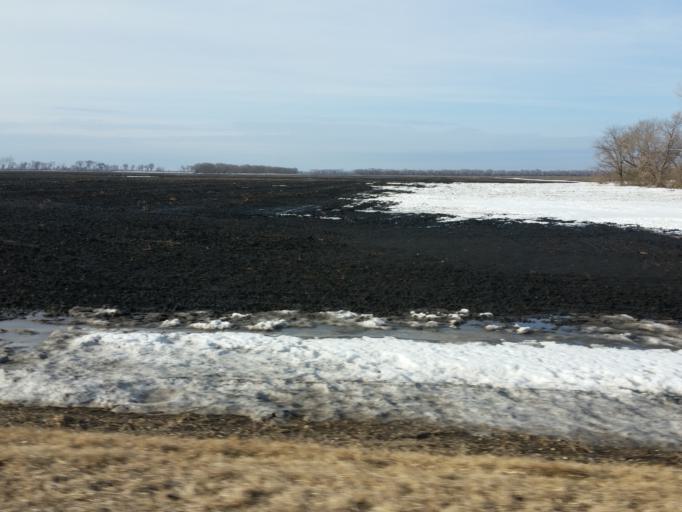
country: US
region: North Dakota
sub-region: Walsh County
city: Grafton
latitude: 48.4266
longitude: -97.2194
